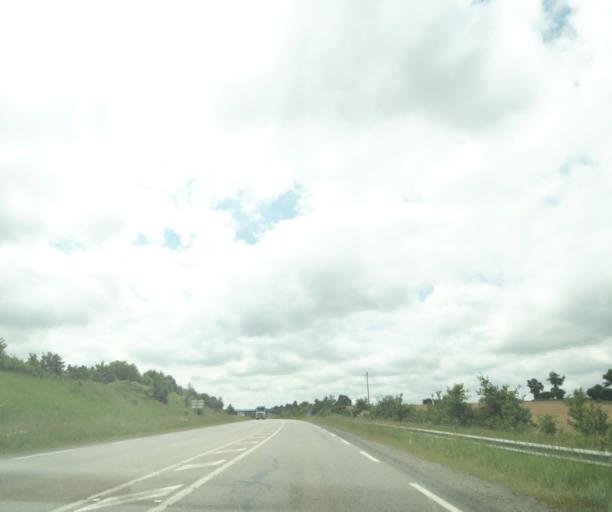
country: FR
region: Poitou-Charentes
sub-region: Departement des Deux-Sevres
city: Parthenay
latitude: 46.6453
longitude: -0.2747
